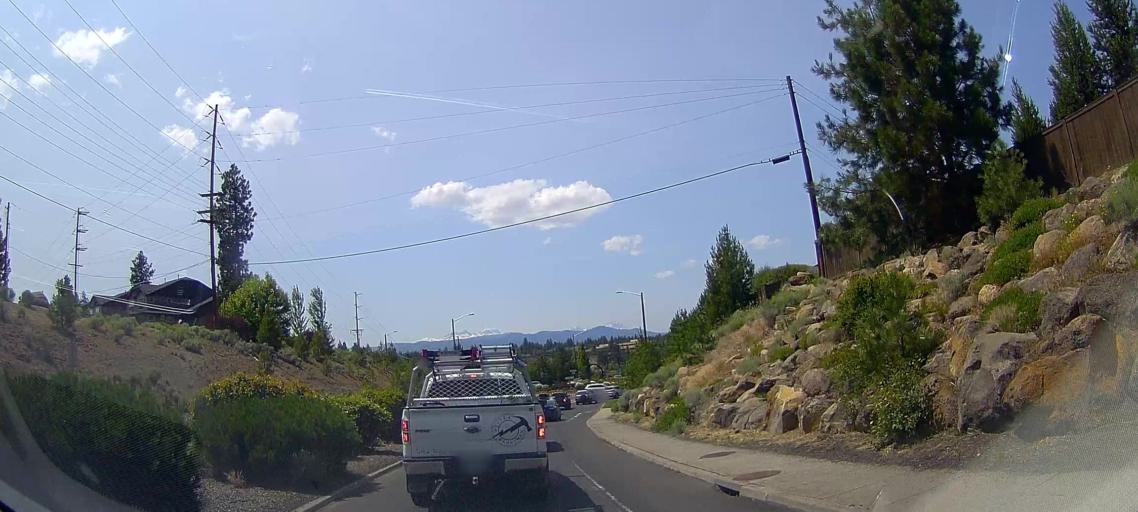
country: US
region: Oregon
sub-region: Deschutes County
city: Bend
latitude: 44.0402
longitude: -121.3156
